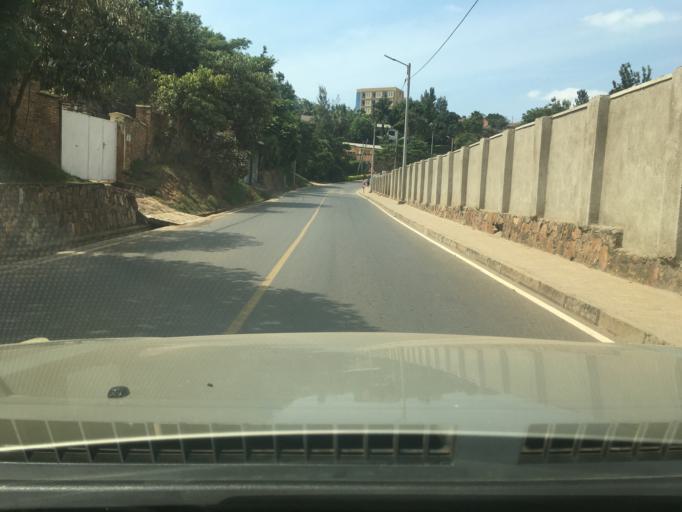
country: RW
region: Kigali
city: Kigali
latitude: -1.9596
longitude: 30.1036
